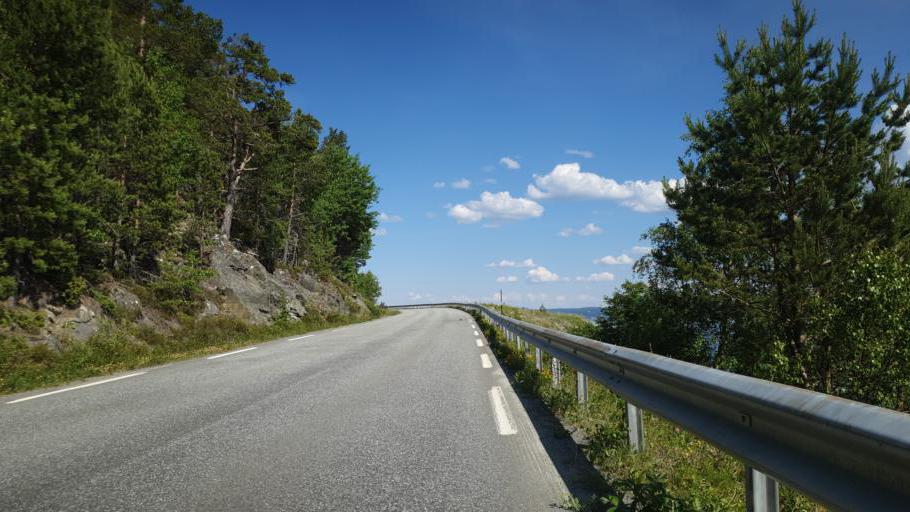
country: NO
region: Nord-Trondelag
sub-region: Leksvik
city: Leksvik
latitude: 63.6260
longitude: 10.5542
